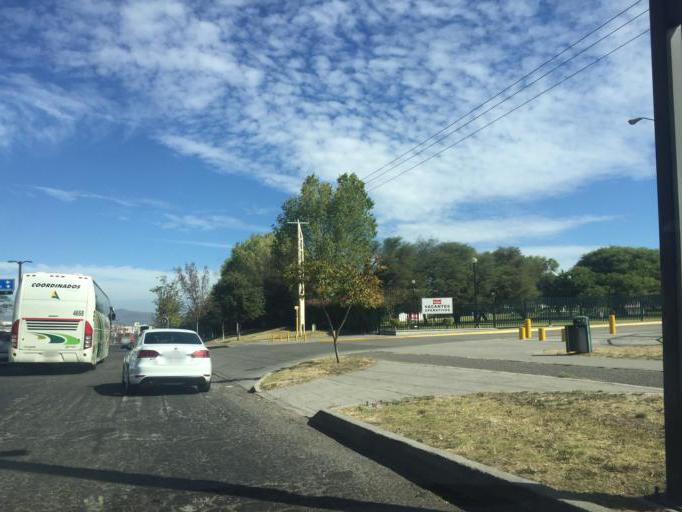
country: MX
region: Queretaro
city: San Juan del Rio
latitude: 20.3792
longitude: -99.9856
